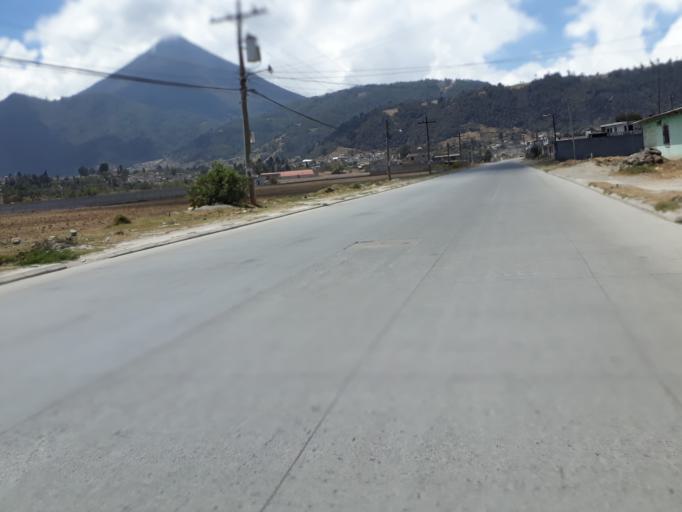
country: GT
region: Quetzaltenango
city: Quetzaltenango
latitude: 14.8154
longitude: -91.5480
